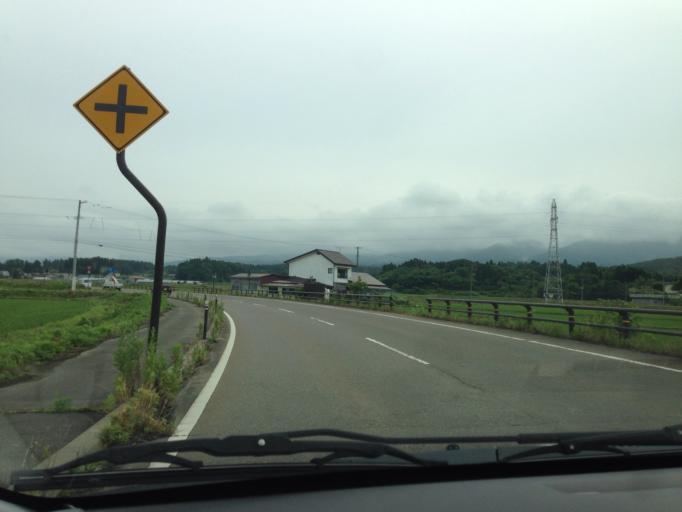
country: JP
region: Fukushima
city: Kitakata
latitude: 37.5924
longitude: 139.9117
